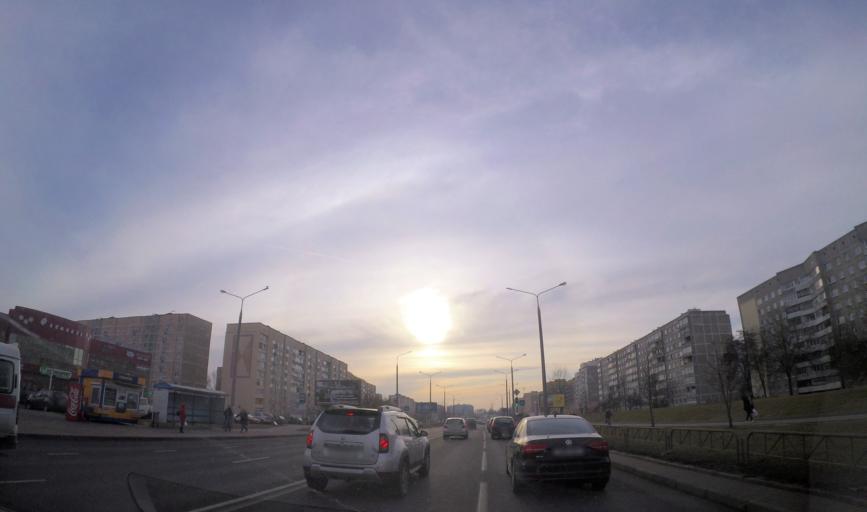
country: BY
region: Grodnenskaya
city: Hrodna
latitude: 53.6638
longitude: 23.7840
